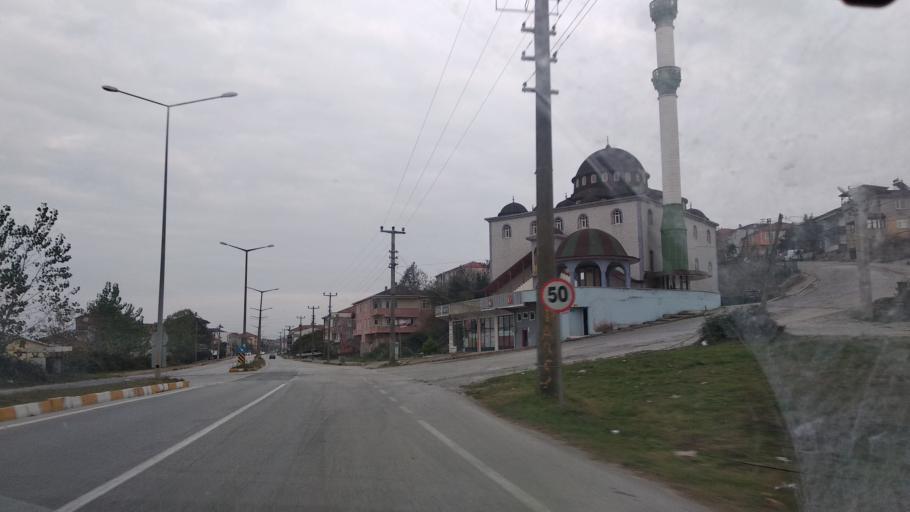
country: TR
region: Sakarya
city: Karasu
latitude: 41.0980
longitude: 30.6744
